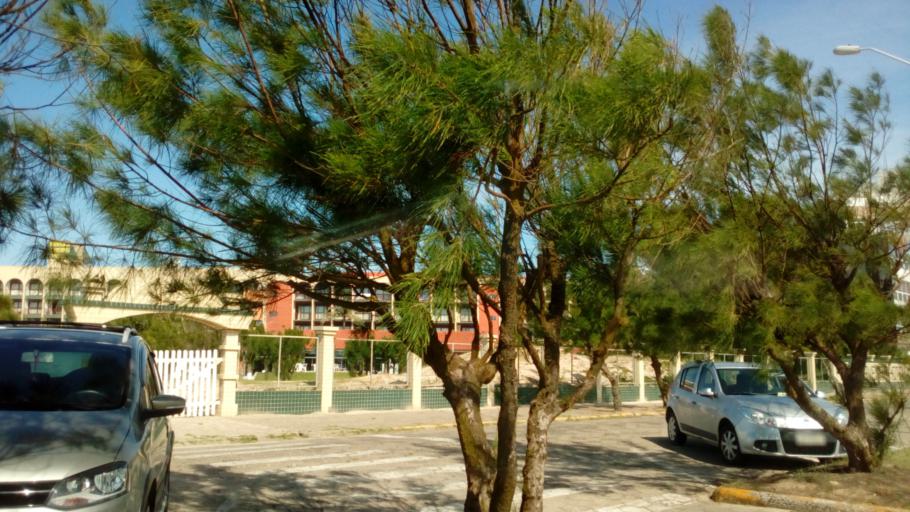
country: BR
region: Santa Catarina
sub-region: Laguna
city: Laguna
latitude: -28.4893
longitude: -48.7648
